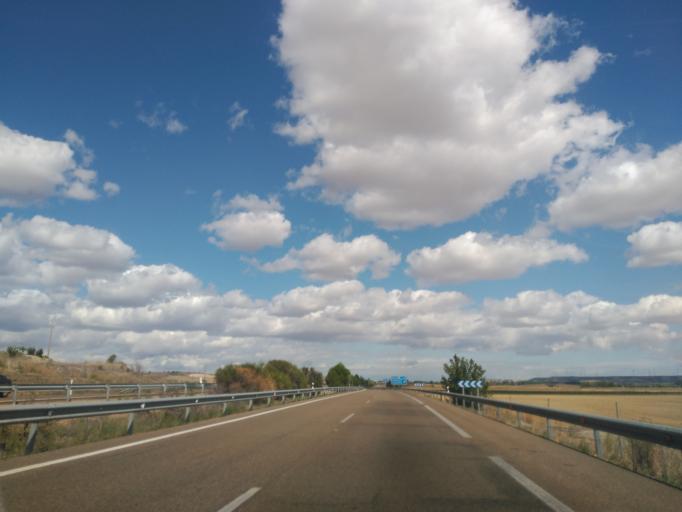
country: ES
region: Castille and Leon
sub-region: Provincia de Palencia
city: Reinoso de Cerrato
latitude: 41.9970
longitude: -4.3876
